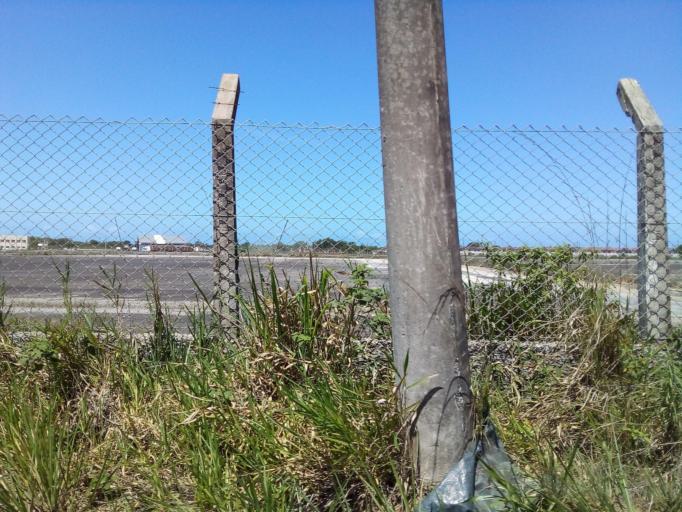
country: BR
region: Espirito Santo
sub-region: Aracruz
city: Aracruz
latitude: -19.8200
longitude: -40.0674
